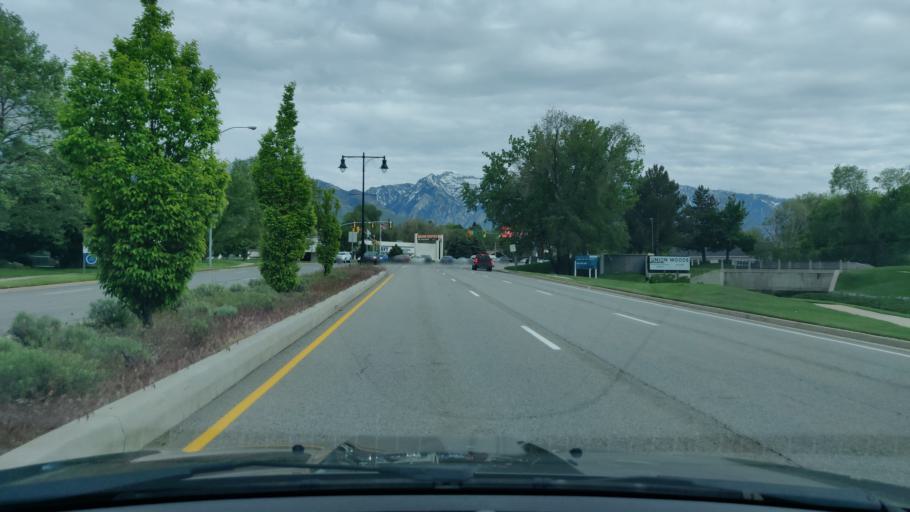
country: US
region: Utah
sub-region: Salt Lake County
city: Little Cottonwood Creek Valley
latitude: 40.6227
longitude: -111.8574
